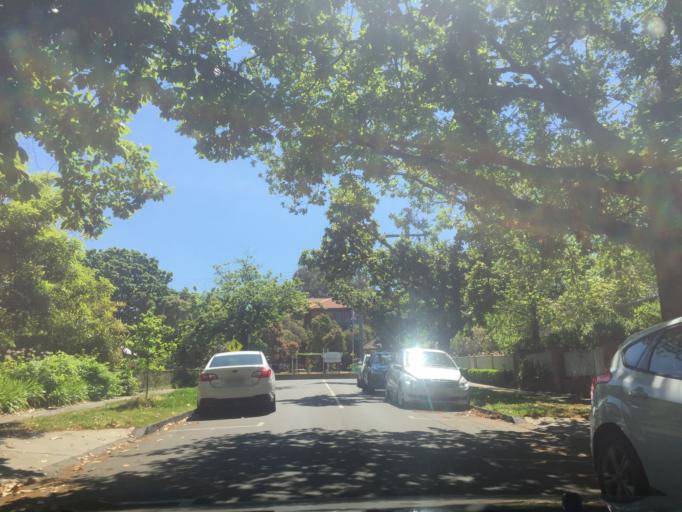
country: AU
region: Victoria
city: Mont Albert
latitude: -37.8182
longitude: 145.0911
